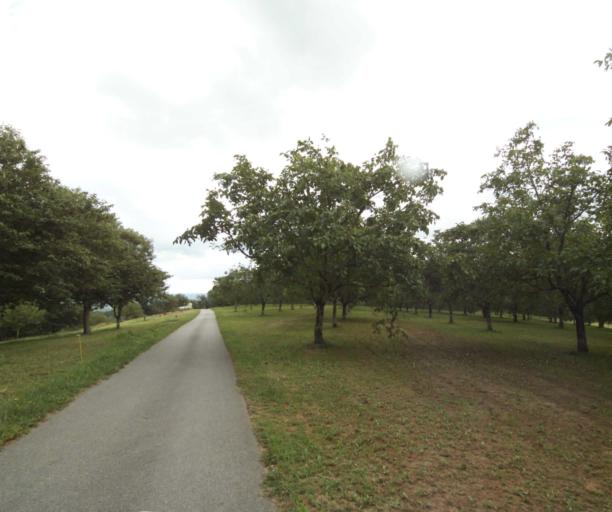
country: FR
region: Limousin
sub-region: Departement de la Correze
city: Sainte-Fortunade
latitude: 45.1730
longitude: 1.8368
